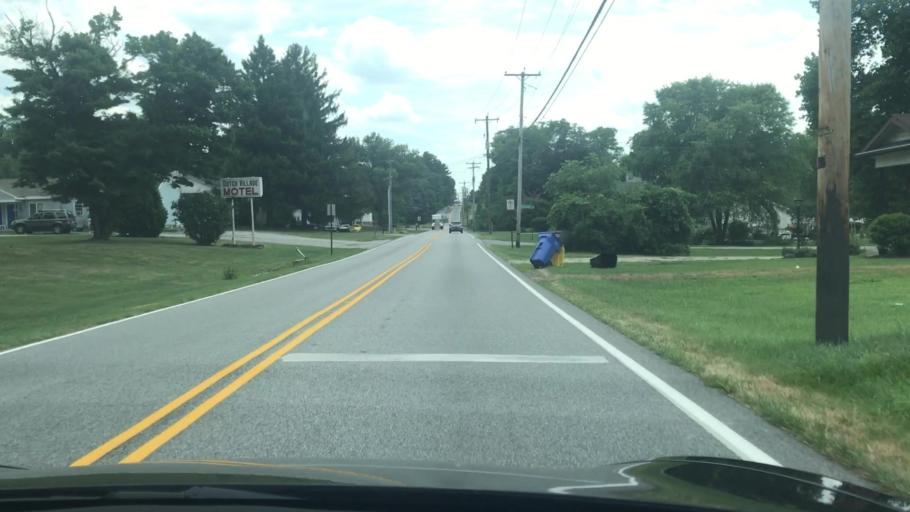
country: US
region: Pennsylvania
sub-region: York County
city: Emigsville
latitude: 40.0321
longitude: -76.7510
